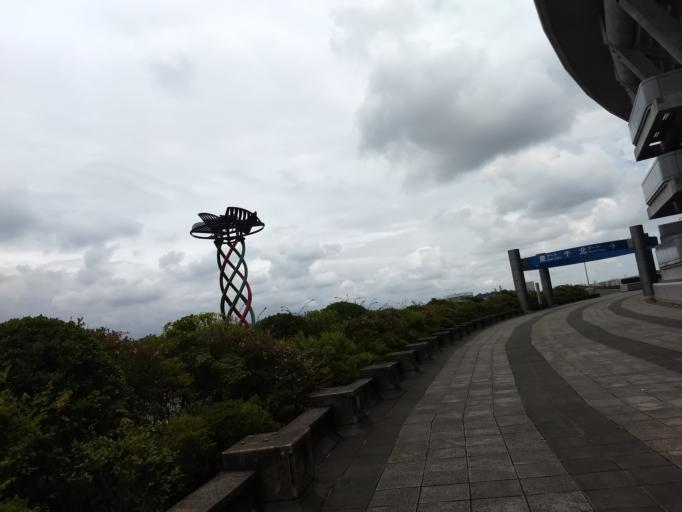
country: JP
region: Kanagawa
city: Yokohama
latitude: 35.5112
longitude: 139.6057
